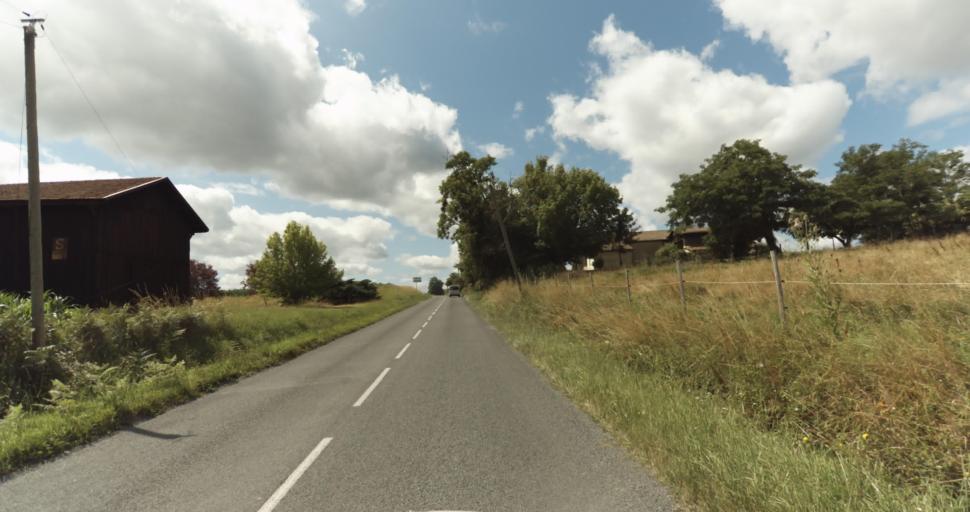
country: FR
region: Aquitaine
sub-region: Departement de la Gironde
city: Bazas
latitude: 44.4491
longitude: -0.2061
